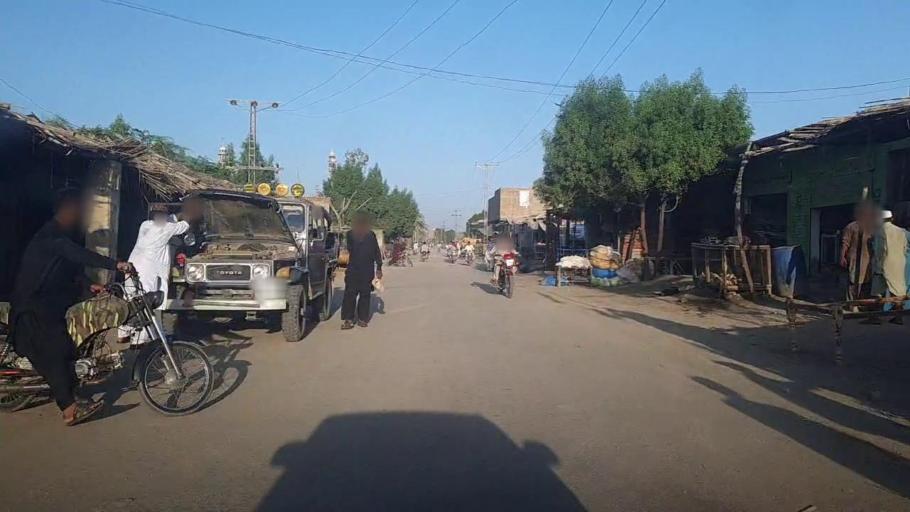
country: PK
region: Sindh
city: Khairpur
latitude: 28.0532
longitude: 69.6931
